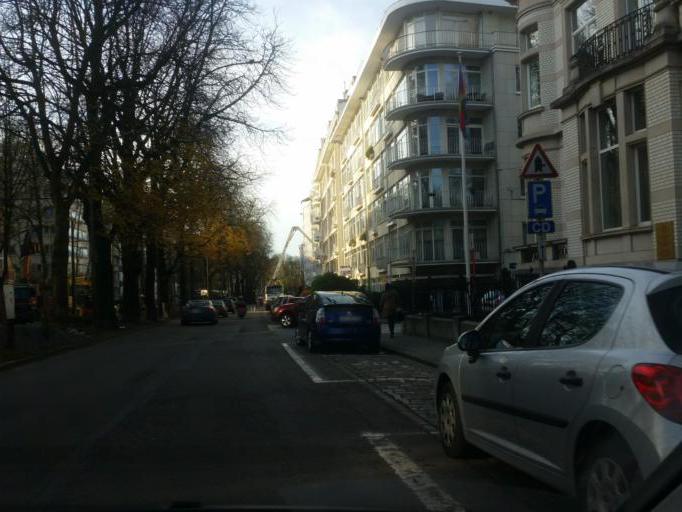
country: BE
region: Brussels Capital
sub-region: Bruxelles-Capitale
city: Brussels
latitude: 50.8115
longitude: 4.3609
